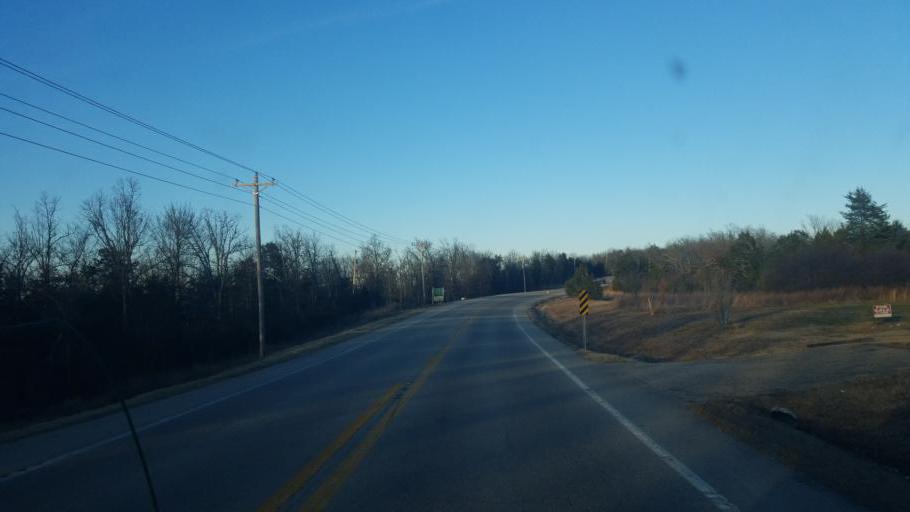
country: US
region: Arkansas
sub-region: Baxter County
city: Mountain Home
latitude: 36.3836
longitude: -92.1913
